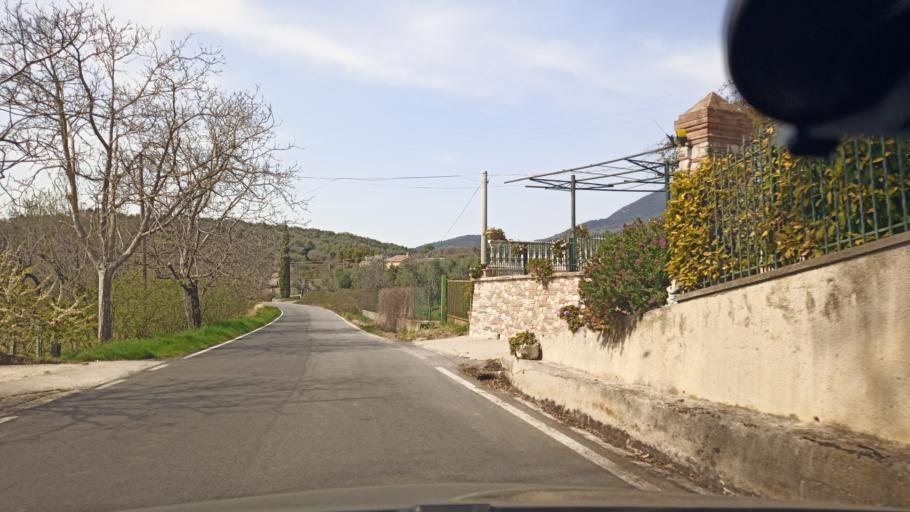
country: IT
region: Latium
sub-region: Provincia di Rieti
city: Vacone
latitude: 42.3649
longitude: 12.6602
